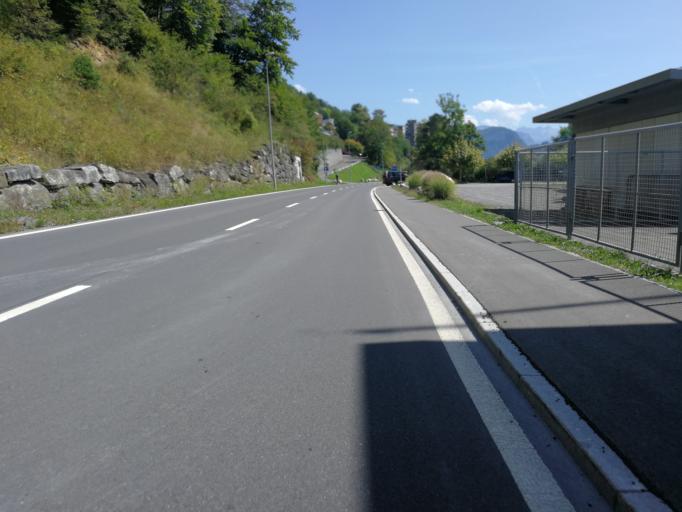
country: CH
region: Schwyz
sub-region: Bezirk Schwyz
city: Ingenbohl
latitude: 47.0011
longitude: 8.5815
